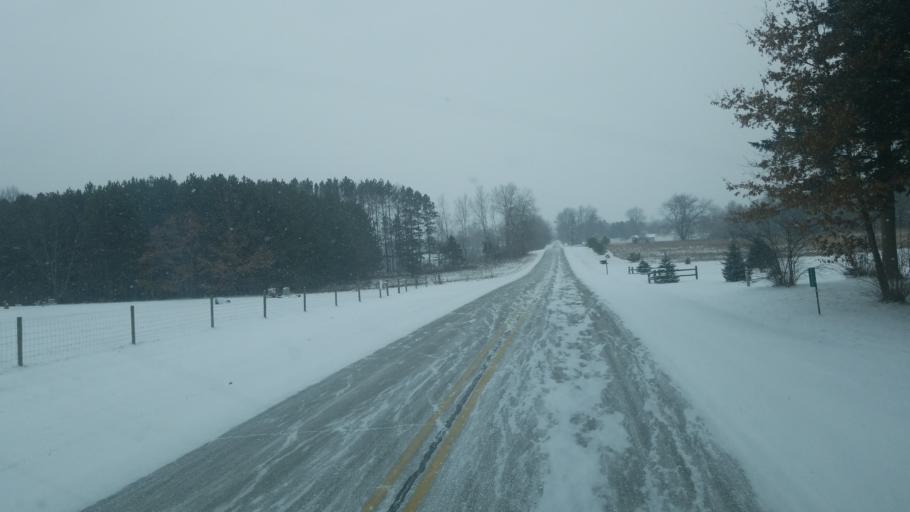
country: US
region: Michigan
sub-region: Mecosta County
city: Big Rapids
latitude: 43.7439
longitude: -85.4033
